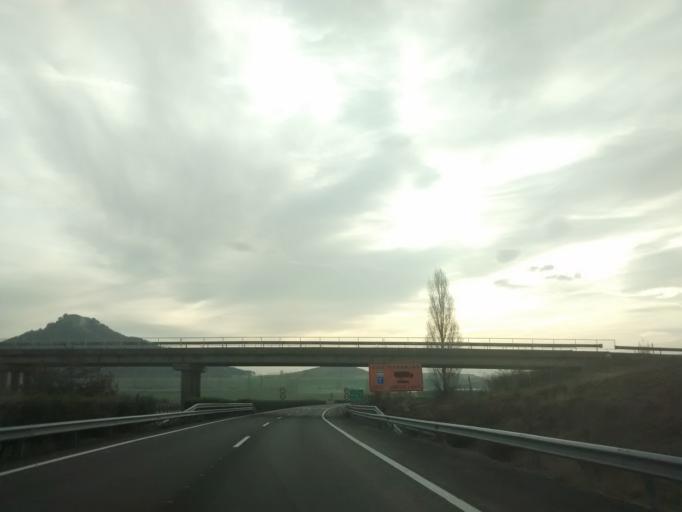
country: ES
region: Navarre
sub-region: Provincia de Navarra
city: Oltza
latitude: 42.8738
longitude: -1.7545
